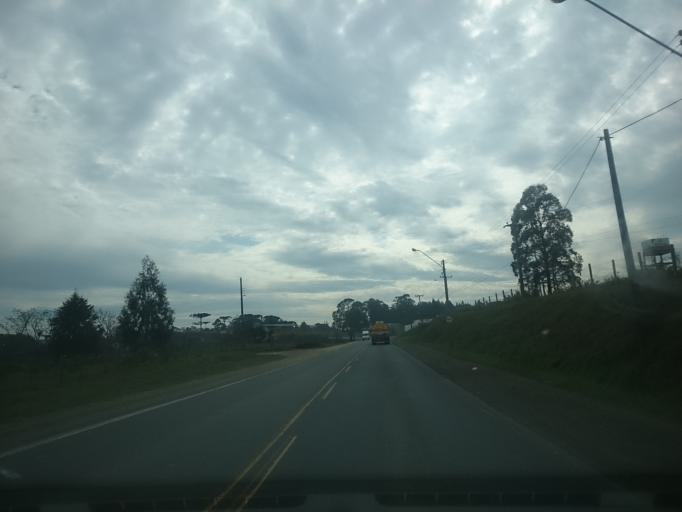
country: BR
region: Santa Catarina
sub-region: Lages
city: Lages
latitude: -27.7781
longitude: -50.3209
